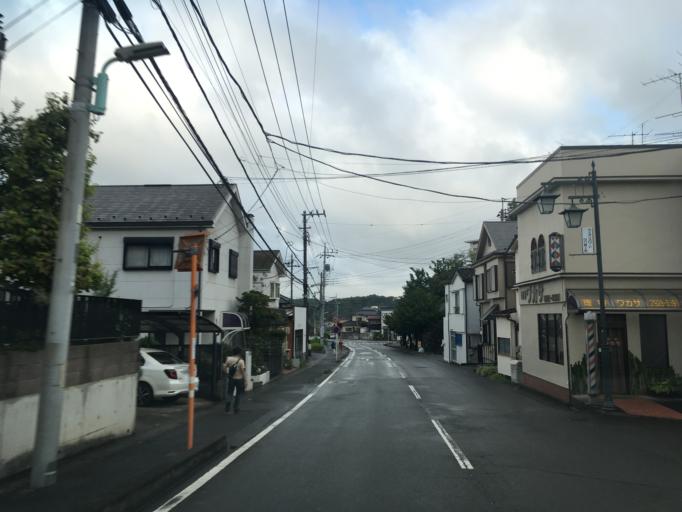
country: JP
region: Saitama
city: Tokorozawa
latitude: 35.7834
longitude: 139.4399
